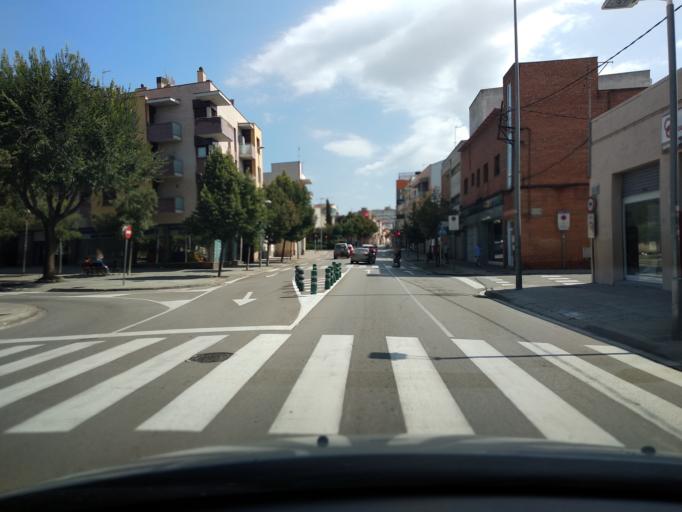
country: ES
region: Catalonia
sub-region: Provincia de Barcelona
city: Granollers
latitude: 41.6107
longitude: 2.2848
